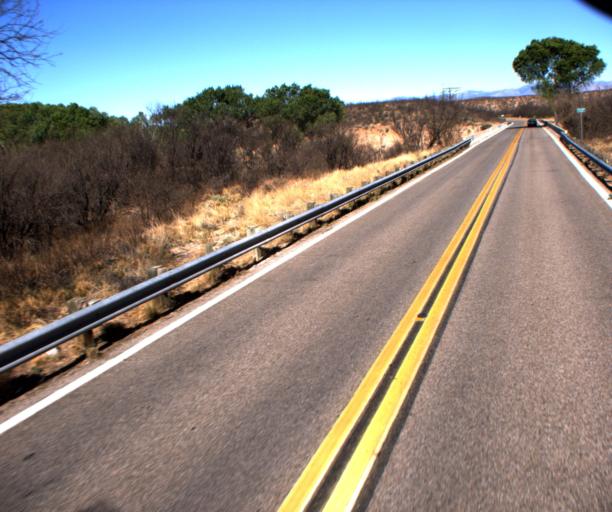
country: US
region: Arizona
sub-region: Cochise County
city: Tombstone
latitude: 31.7228
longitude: -110.1925
